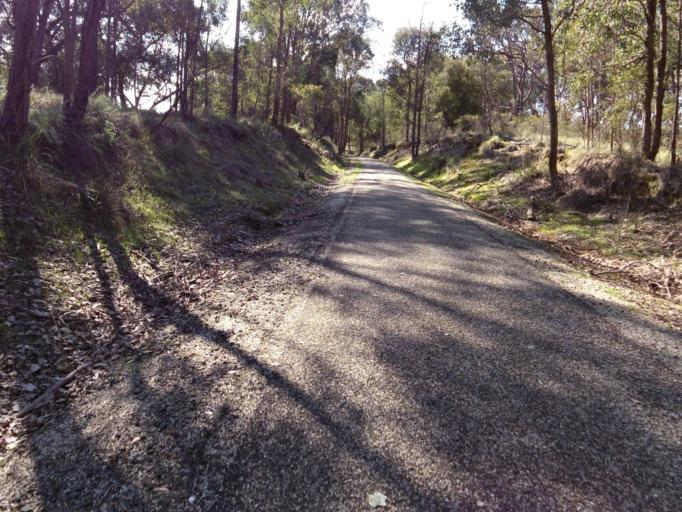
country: AU
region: Victoria
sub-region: Wangaratta
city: Wangaratta
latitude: -36.4029
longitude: 146.6406
